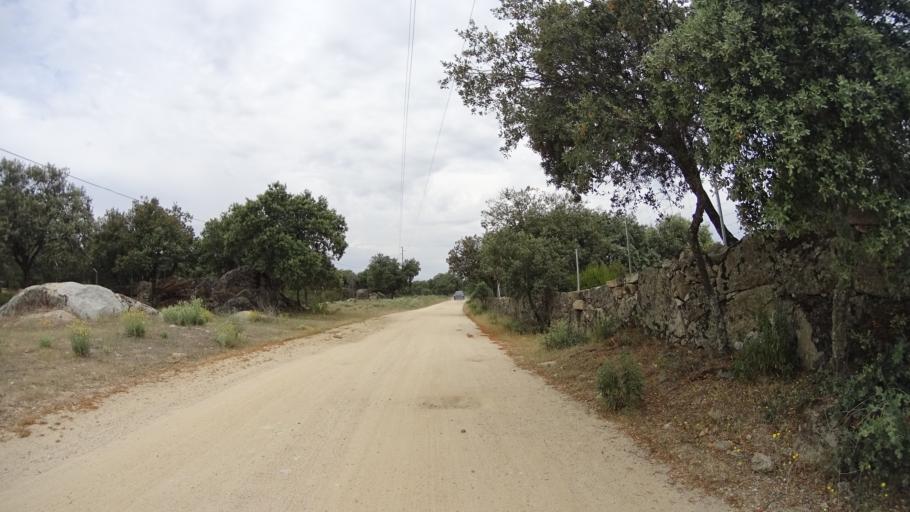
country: ES
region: Madrid
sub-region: Provincia de Madrid
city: Colmenarejo
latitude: 40.5544
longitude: -4.0373
